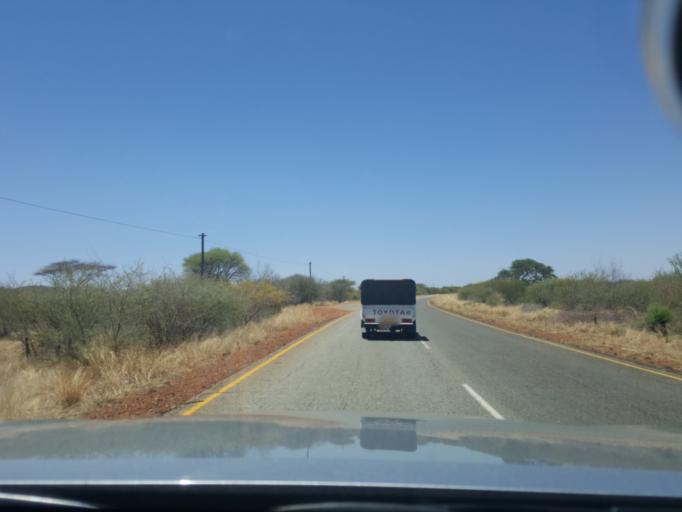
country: BW
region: South East
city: Otse
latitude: -25.0960
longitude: 25.9618
